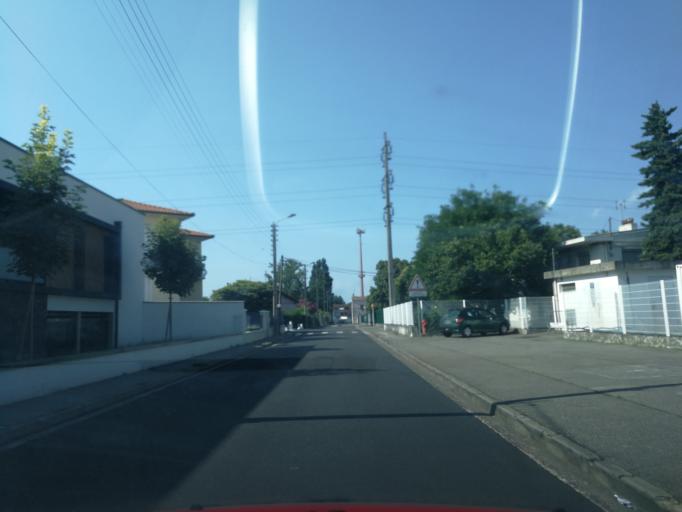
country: FR
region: Midi-Pyrenees
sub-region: Departement de la Haute-Garonne
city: Blagnac
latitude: 43.6209
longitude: 1.4082
